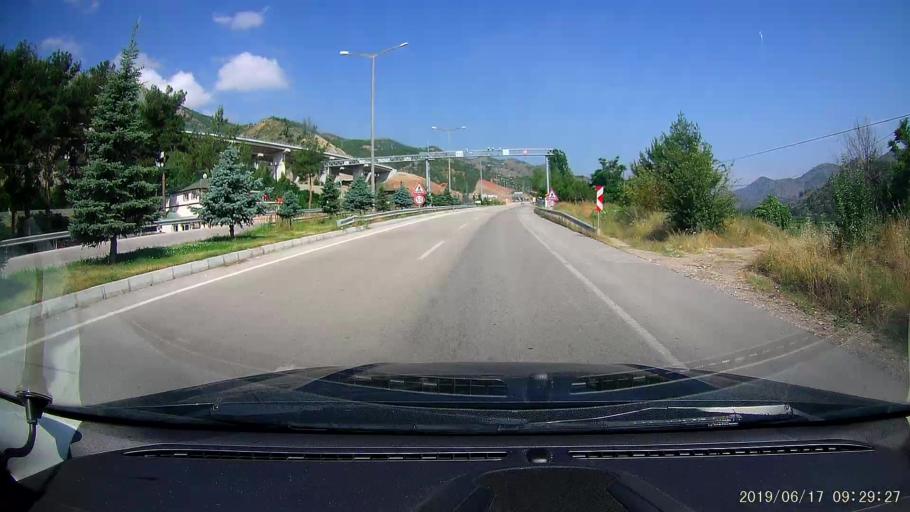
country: TR
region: Amasya
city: Amasya
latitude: 40.6966
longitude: 35.8121
